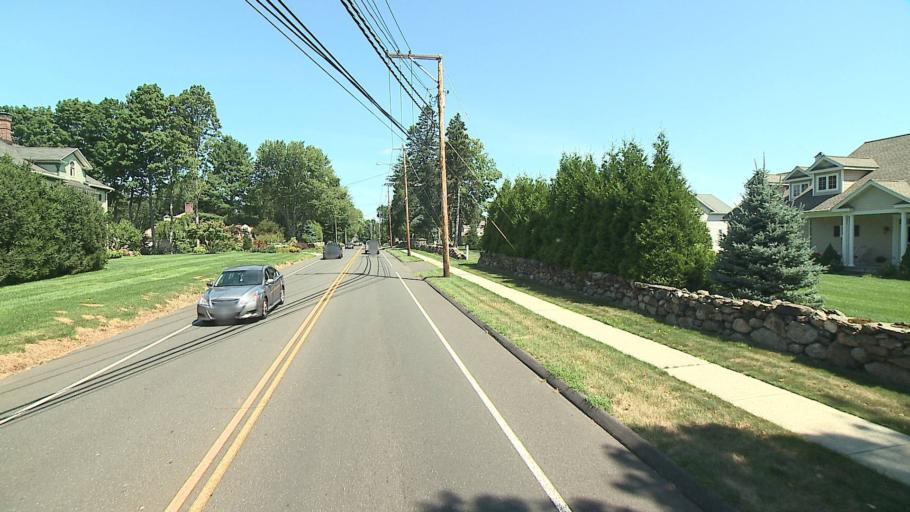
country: US
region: Connecticut
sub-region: Fairfield County
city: Trumbull
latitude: 41.2448
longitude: -73.2215
